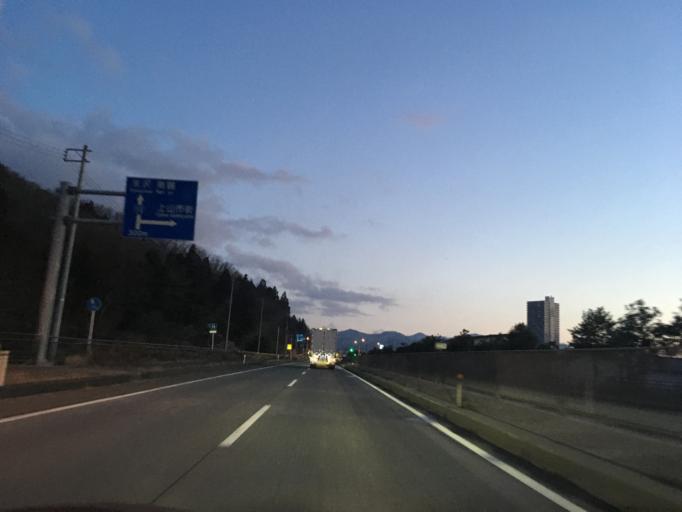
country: JP
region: Yamagata
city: Kaminoyama
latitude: 38.1460
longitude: 140.2889
